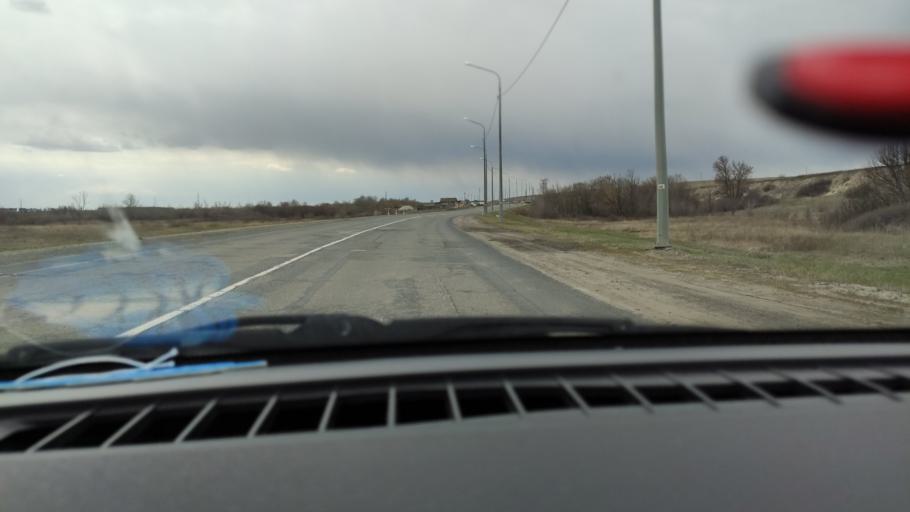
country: RU
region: Saratov
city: Sinodskoye
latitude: 52.0876
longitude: 46.8051
